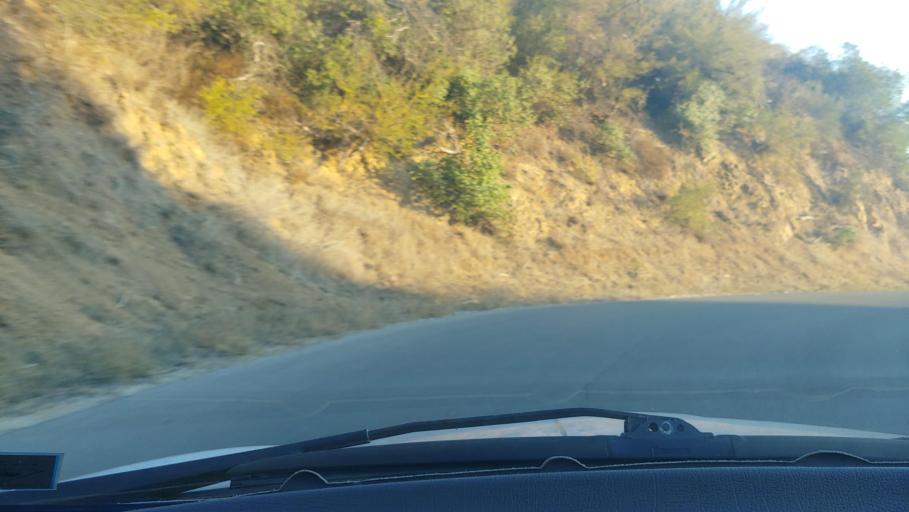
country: US
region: California
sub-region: Santa Barbara County
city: Mission Canyon
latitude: 34.4704
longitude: -119.6778
